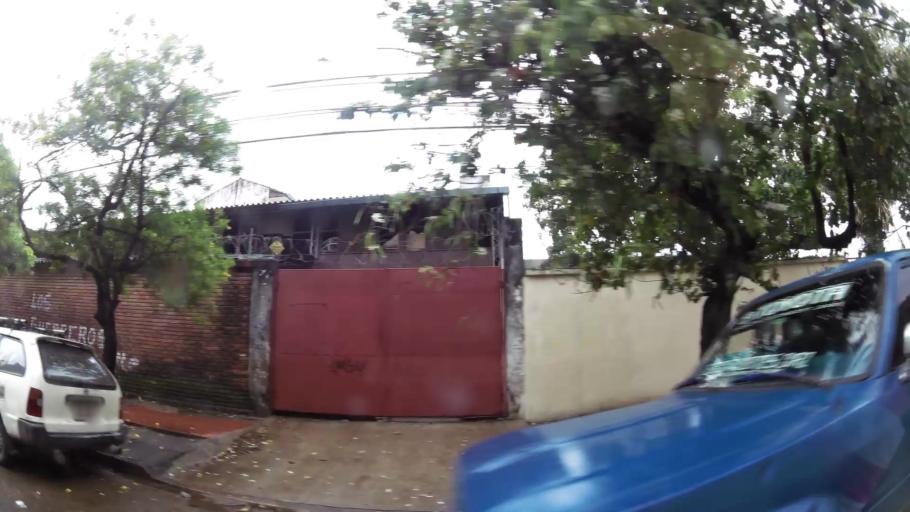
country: BO
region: Santa Cruz
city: Santa Cruz de la Sierra
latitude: -17.8057
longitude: -63.1870
